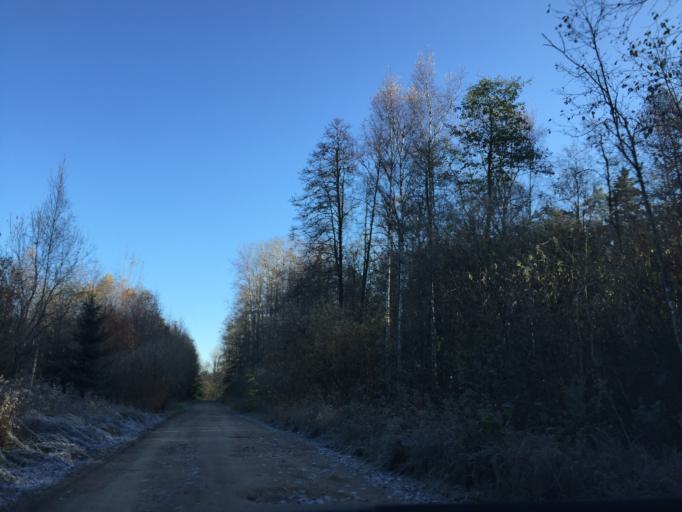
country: LV
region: Aizkraukles Rajons
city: Aizkraukle
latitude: 56.7046
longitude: 25.2859
